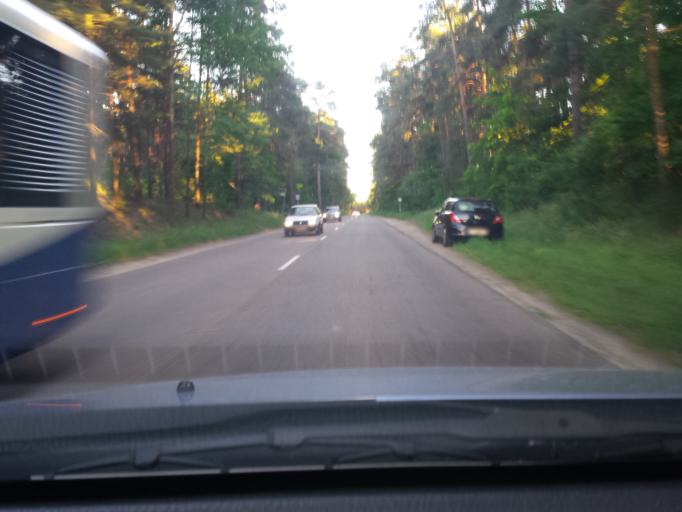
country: LV
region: Riga
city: Jaunciems
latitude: 57.0326
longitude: 24.1873
